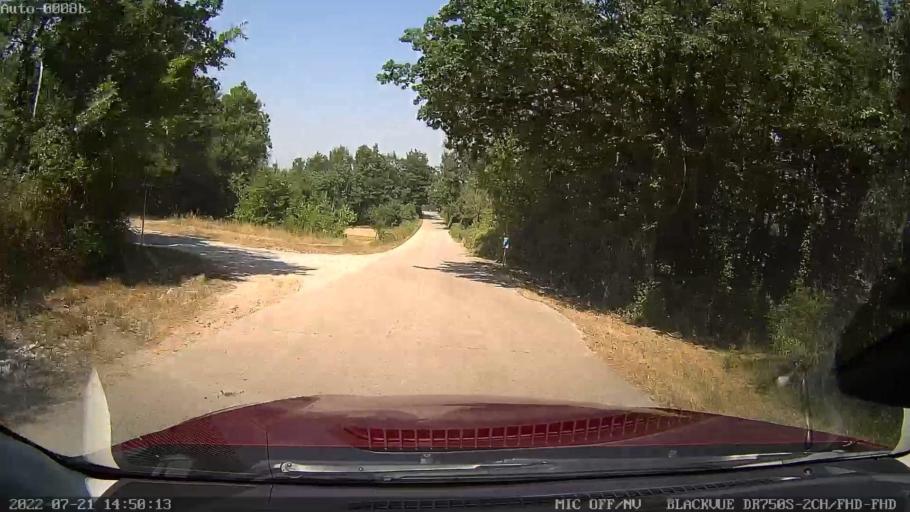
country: HR
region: Istarska
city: Pazin
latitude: 45.1584
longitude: 13.9142
